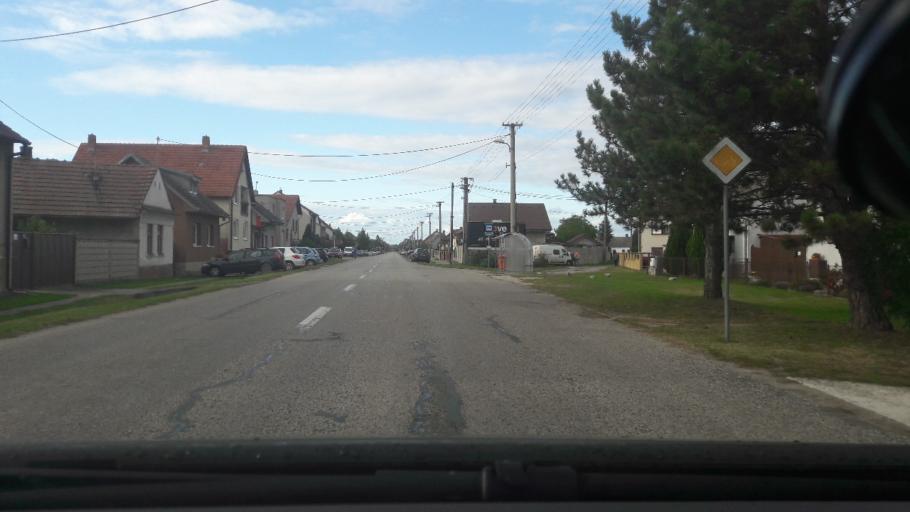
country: CZ
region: South Moravian
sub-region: Okres Breclav
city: Lanzhot
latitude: 48.6628
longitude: 17.0126
